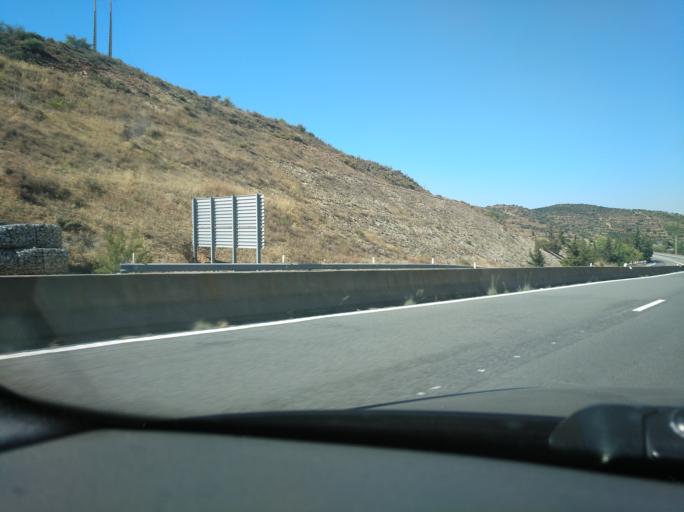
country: PT
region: Faro
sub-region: Tavira
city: Tavira
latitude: 37.1488
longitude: -7.6722
